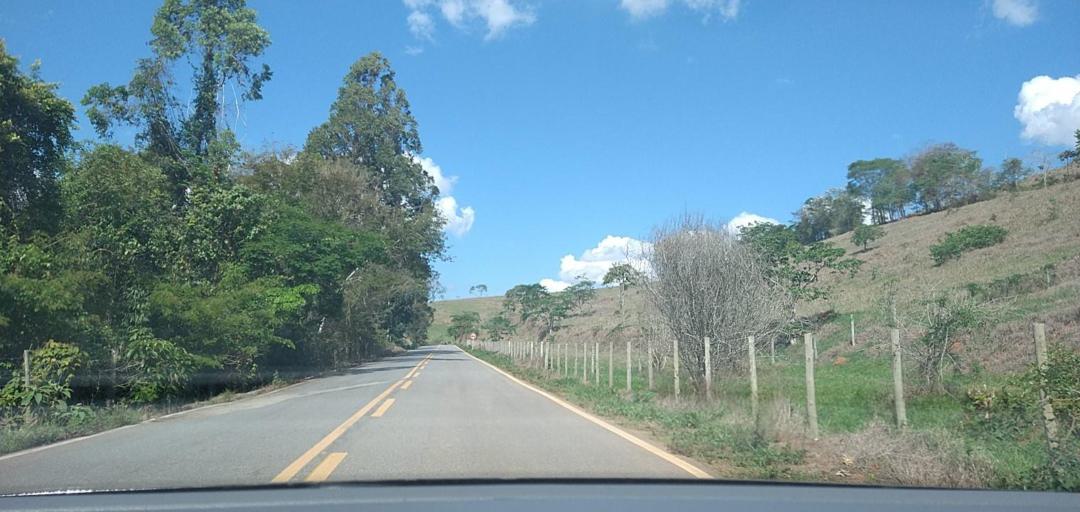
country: BR
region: Minas Gerais
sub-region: Alvinopolis
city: Alvinopolis
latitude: -20.0169
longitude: -43.0914
